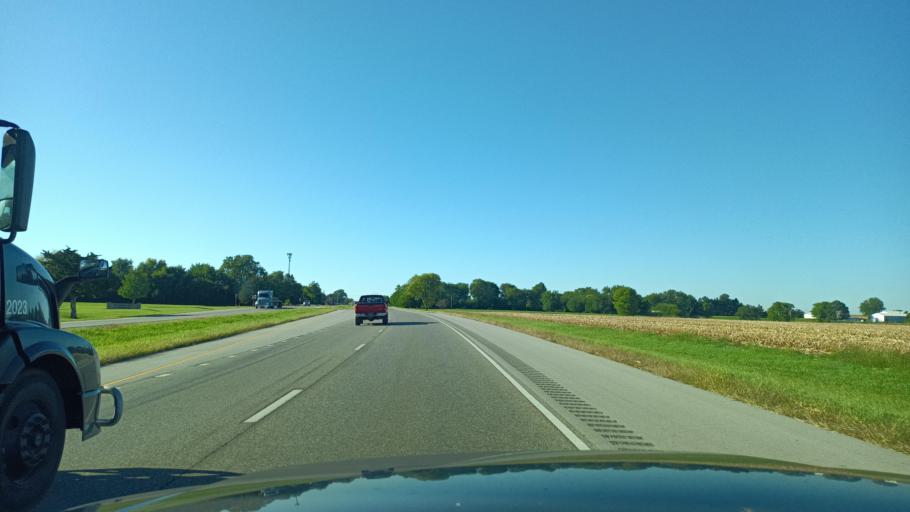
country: US
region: Illinois
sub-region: Warren County
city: Monmouth
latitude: 40.9184
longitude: -90.6634
